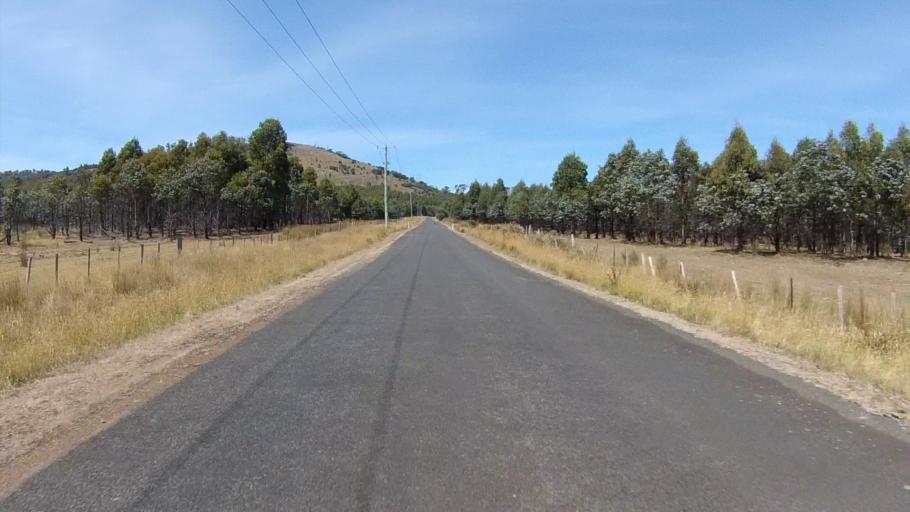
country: AU
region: Tasmania
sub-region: Sorell
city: Sorell
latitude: -42.6203
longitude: 147.7299
